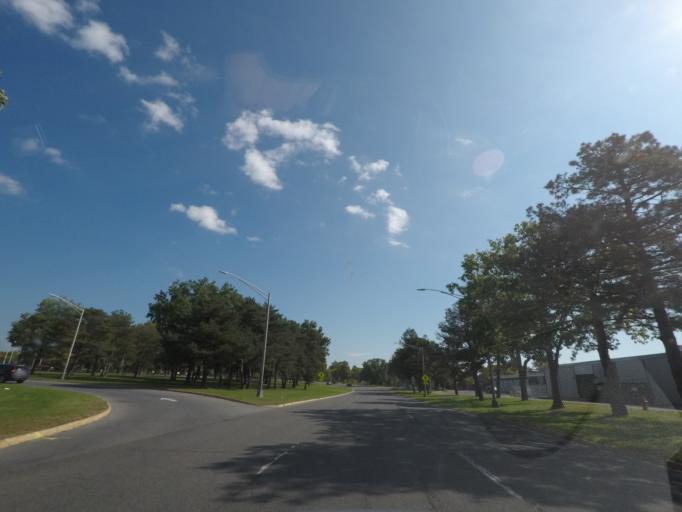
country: US
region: New York
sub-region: Albany County
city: Roessleville
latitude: 42.6750
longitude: -73.8101
